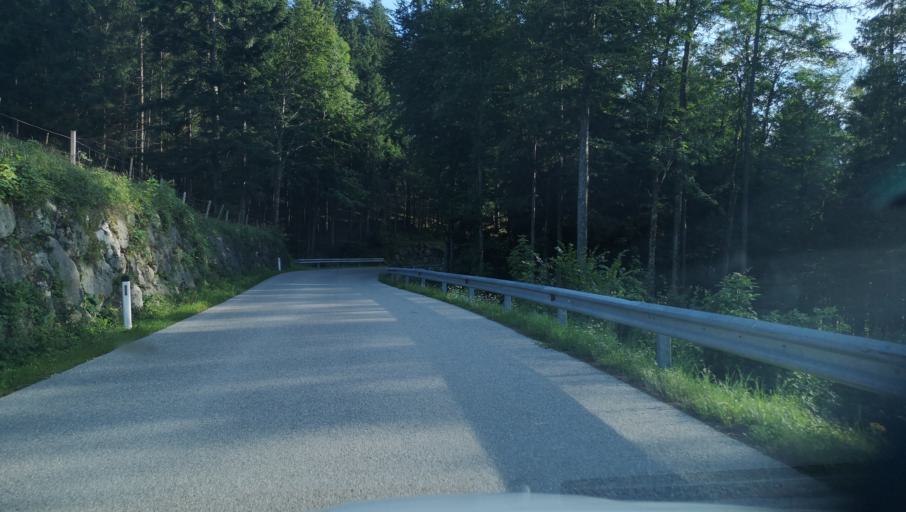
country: AT
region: Lower Austria
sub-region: Politischer Bezirk Amstetten
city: Ybbsitz
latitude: 47.9850
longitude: 14.8485
